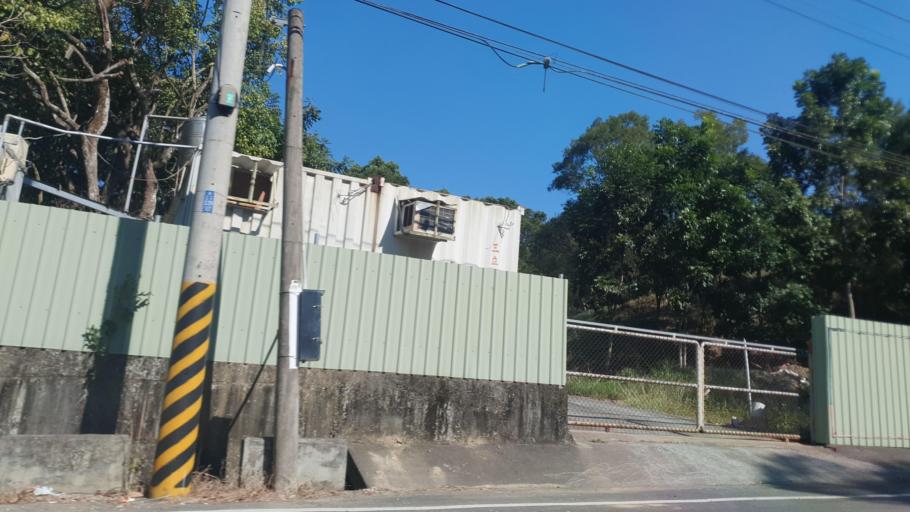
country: TW
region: Taiwan
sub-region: Tainan
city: Tainan
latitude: 23.0344
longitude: 120.3460
